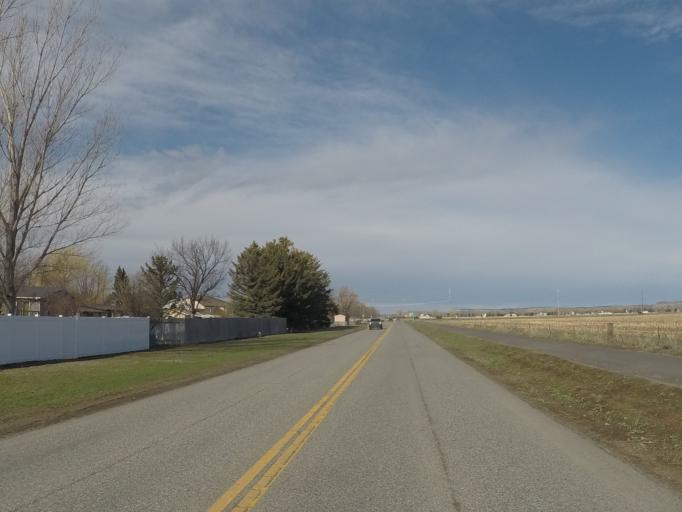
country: US
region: Montana
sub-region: Yellowstone County
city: Billings
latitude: 45.7769
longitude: -108.6121
